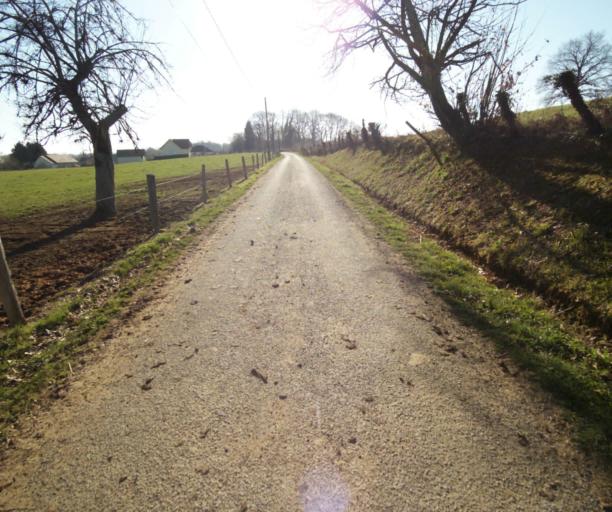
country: FR
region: Limousin
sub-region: Departement de la Correze
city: Saint-Clement
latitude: 45.3905
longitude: 1.6361
